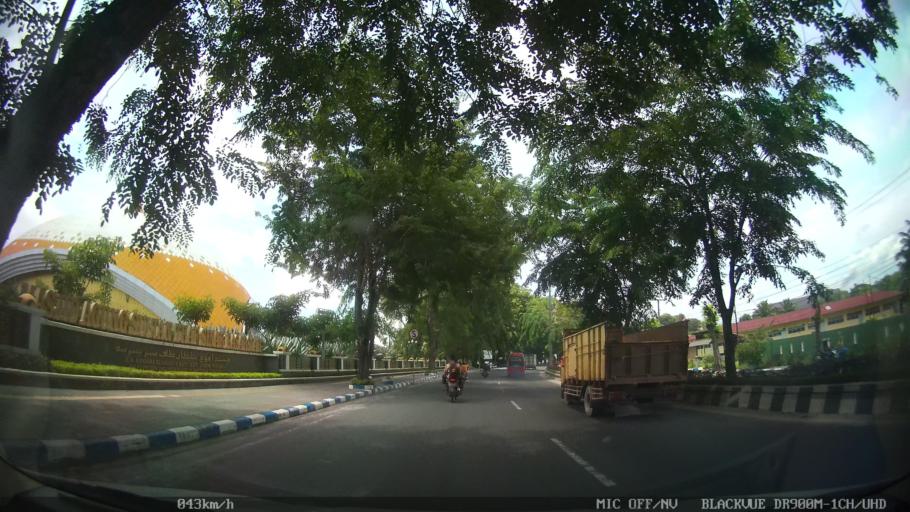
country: ID
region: North Sumatra
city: Percut
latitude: 3.5528
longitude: 98.8700
